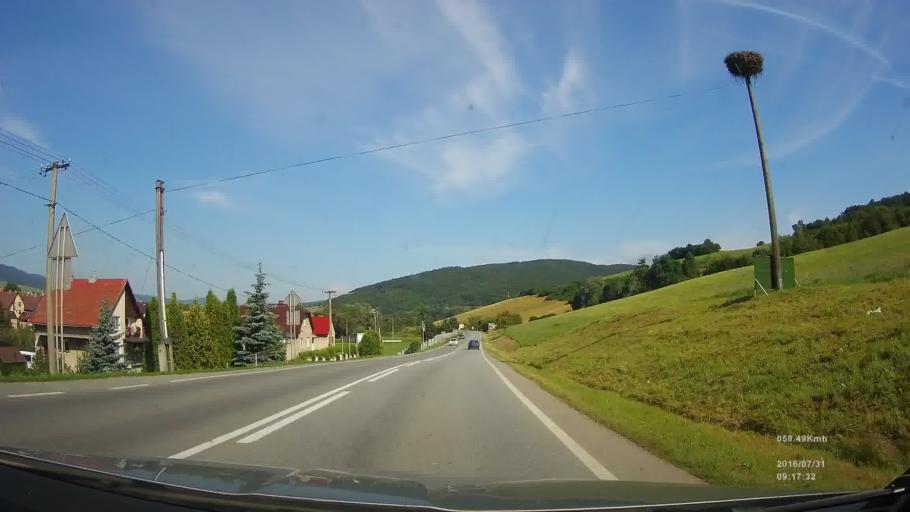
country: SK
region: Presovsky
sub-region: Okres Bardejov
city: Bardejov
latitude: 49.2489
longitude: 21.2565
